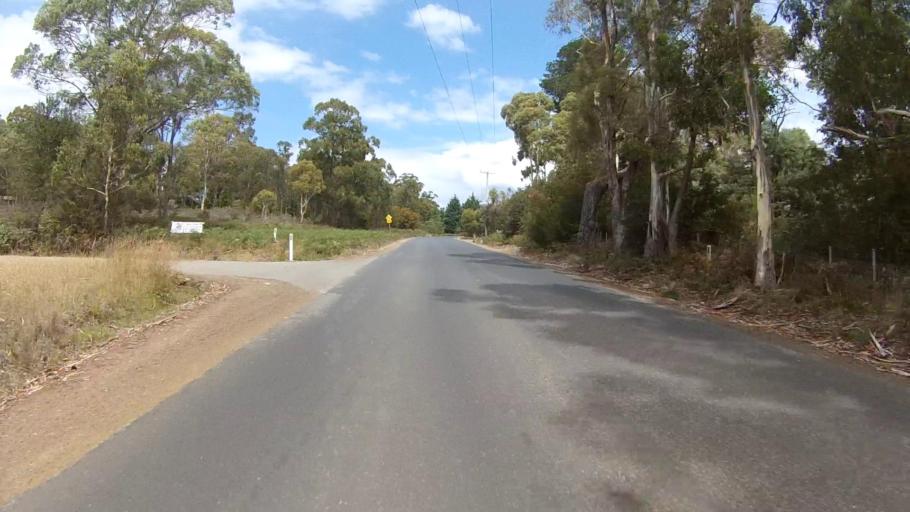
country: AU
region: Tasmania
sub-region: Kingborough
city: Blackmans Bay
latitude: -43.0110
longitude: 147.2882
